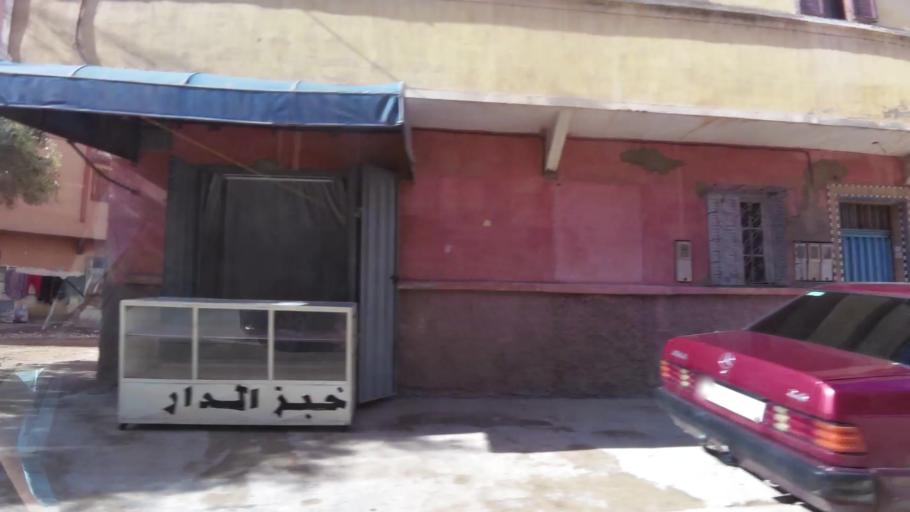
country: MA
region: Chaouia-Ouardigha
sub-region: Settat Province
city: Berrechid
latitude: 33.2741
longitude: -7.5751
